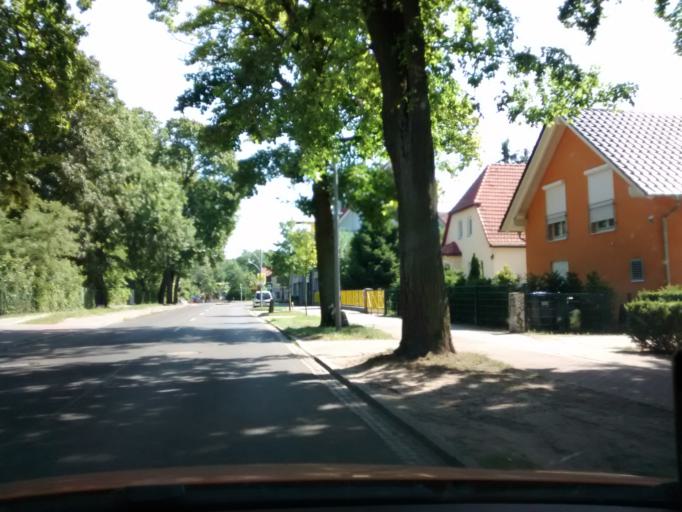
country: DE
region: Brandenburg
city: Hohen Neuendorf
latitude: 52.6635
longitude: 13.2850
